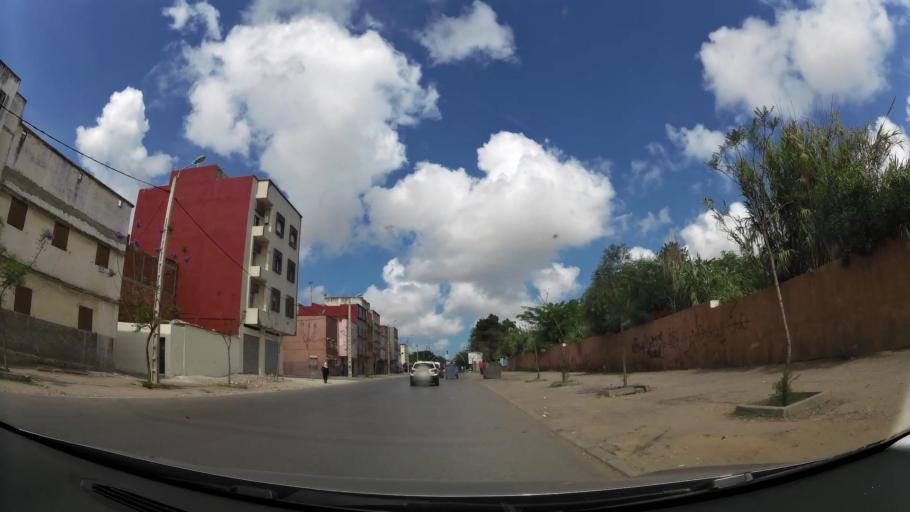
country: MA
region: Gharb-Chrarda-Beni Hssen
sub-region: Kenitra Province
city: Kenitra
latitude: 34.2602
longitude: -6.5608
